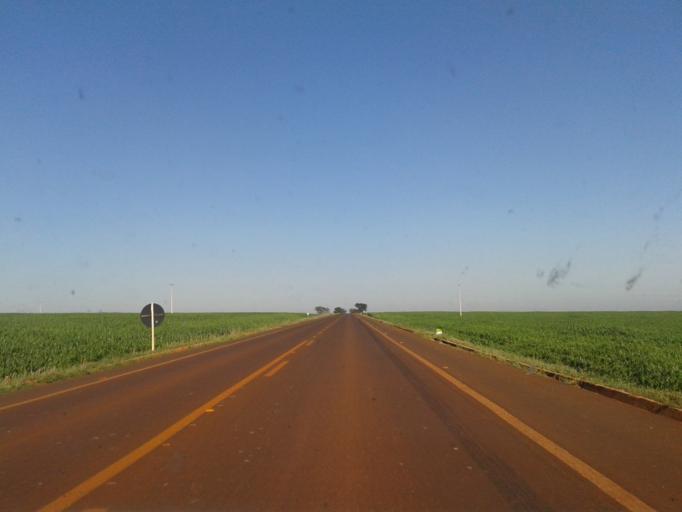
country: BR
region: Minas Gerais
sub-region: Capinopolis
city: Capinopolis
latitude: -18.6975
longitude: -49.6360
